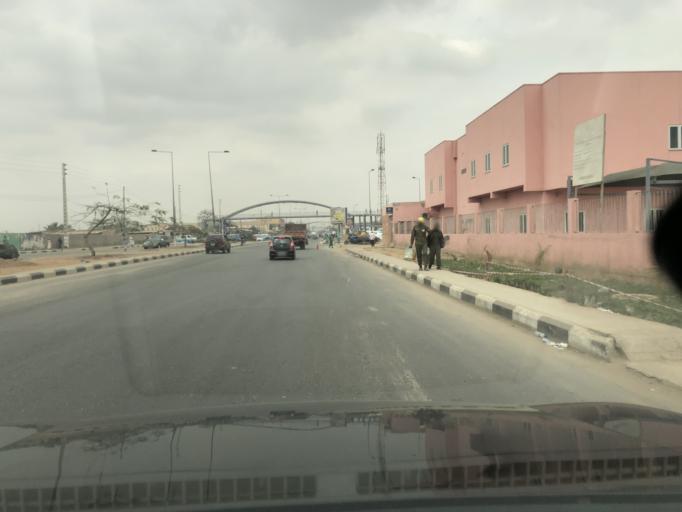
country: AO
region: Luanda
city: Luanda
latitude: -8.8354
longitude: 13.2833
